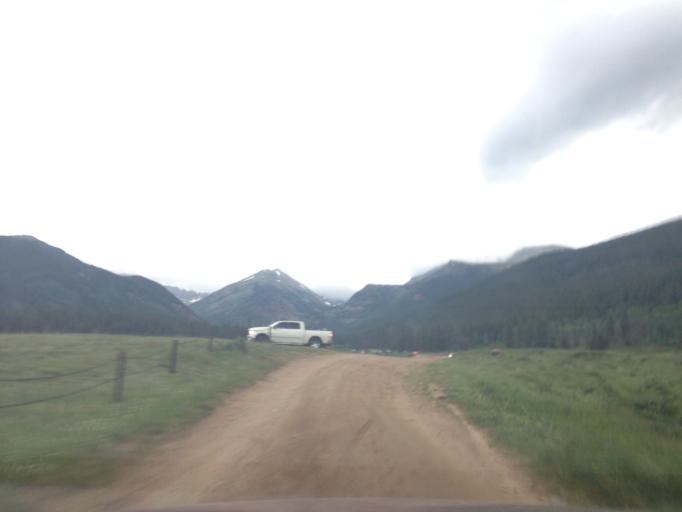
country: US
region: Colorado
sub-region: Clear Creek County
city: Georgetown
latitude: 39.5389
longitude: -105.7432
